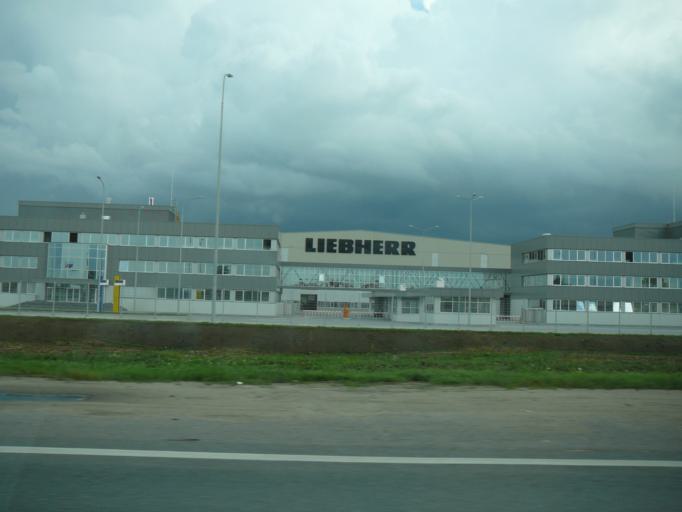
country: RU
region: Nizjnij Novgorod
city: Dzerzhinsk
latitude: 56.2968
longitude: 43.4406
